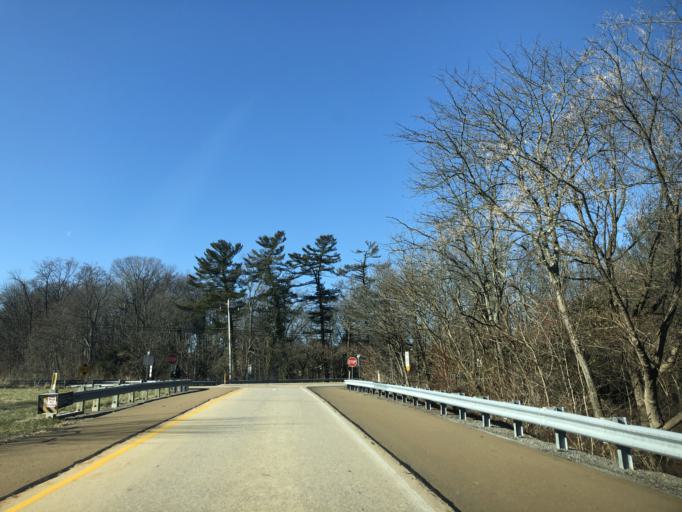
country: US
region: Pennsylvania
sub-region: Chester County
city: Kennett Square
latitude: 39.8572
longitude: -75.7148
